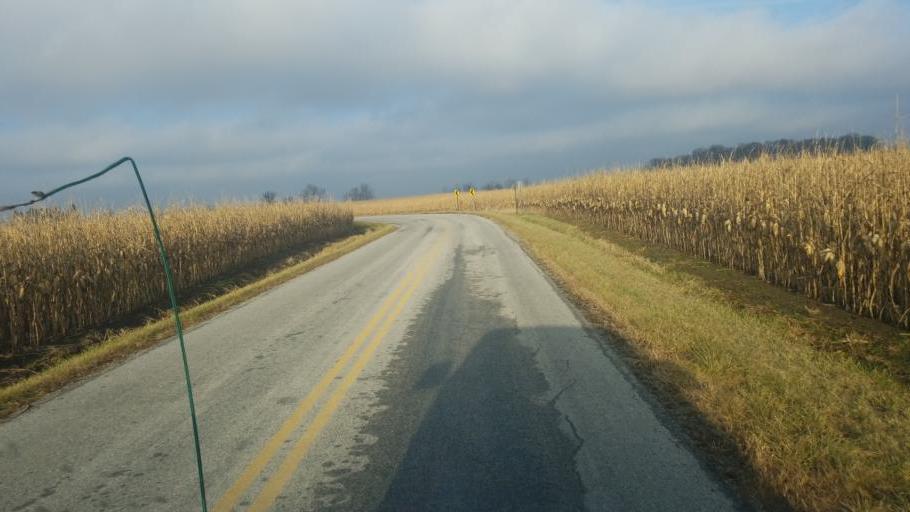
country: US
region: Ohio
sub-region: Hardin County
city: Kenton
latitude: 40.6932
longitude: -83.5942
